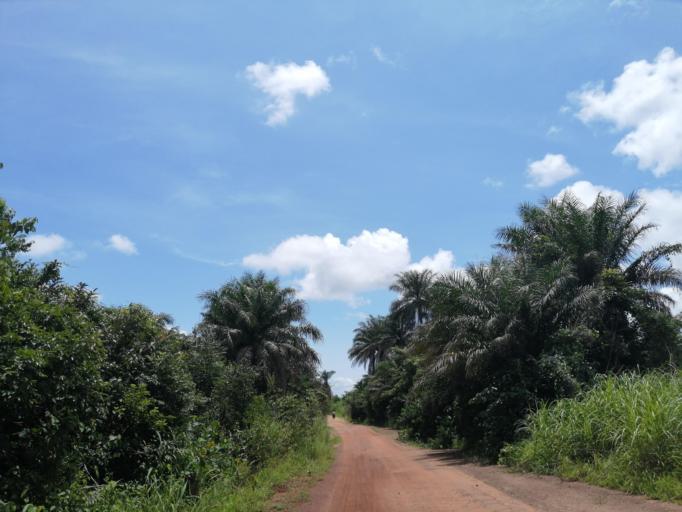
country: SL
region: Northern Province
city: Pepel
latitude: 8.6684
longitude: -13.0005
